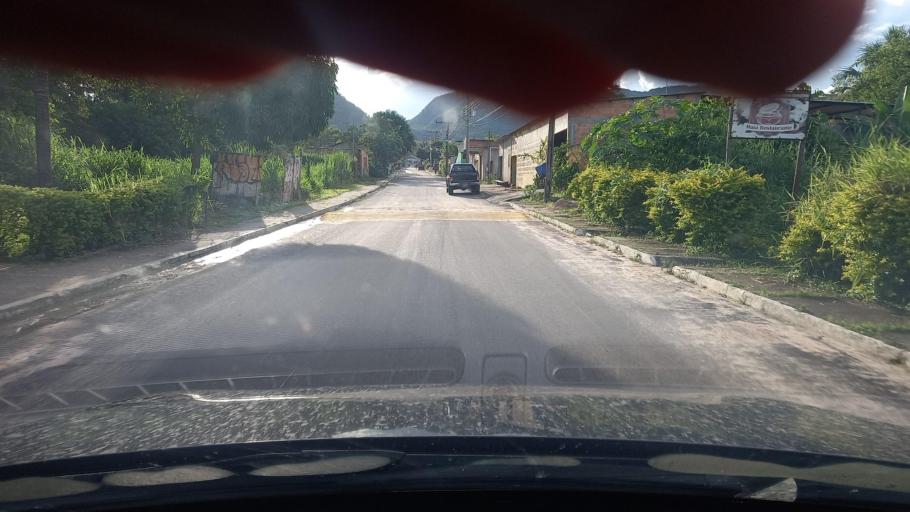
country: BR
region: Goias
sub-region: Cavalcante
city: Cavalcante
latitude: -13.7970
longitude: -47.4566
